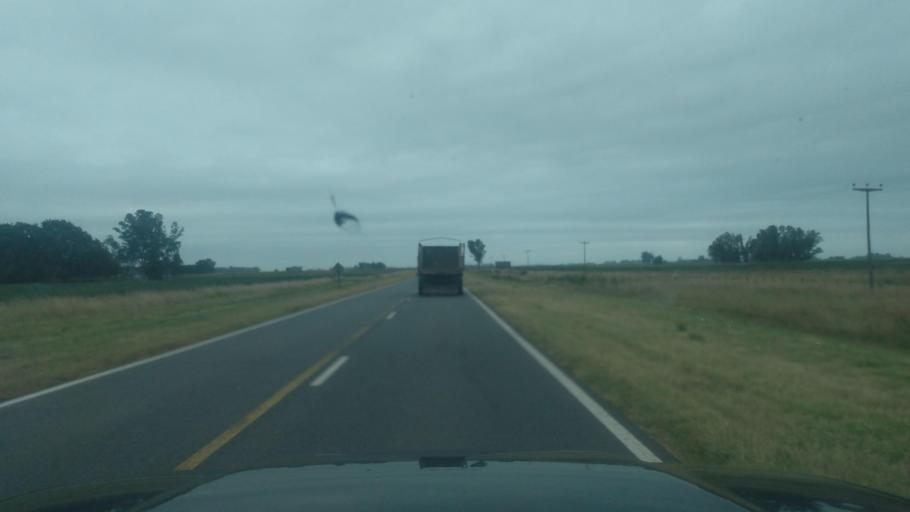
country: AR
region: Buenos Aires
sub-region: Partido de Nueve de Julio
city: Nueve de Julio
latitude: -35.3946
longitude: -60.7424
